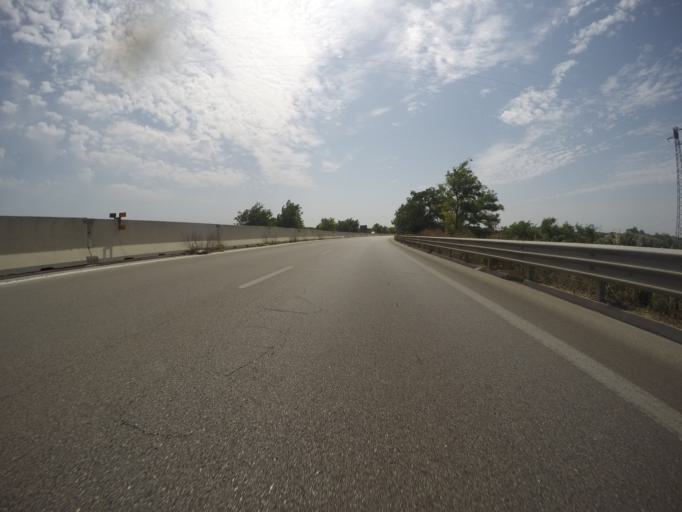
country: IT
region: Apulia
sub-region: Provincia di Brindisi
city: Francavilla Fontana
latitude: 40.5456
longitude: 17.5954
